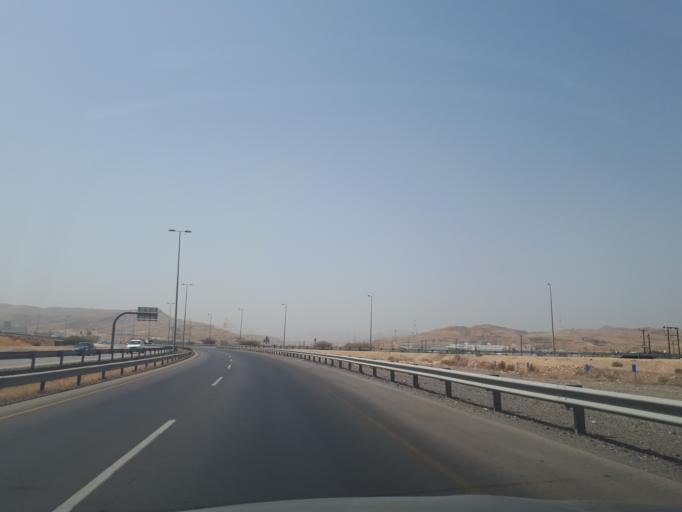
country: OM
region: Muhafazat Masqat
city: As Sib al Jadidah
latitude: 23.5642
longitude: 58.1893
